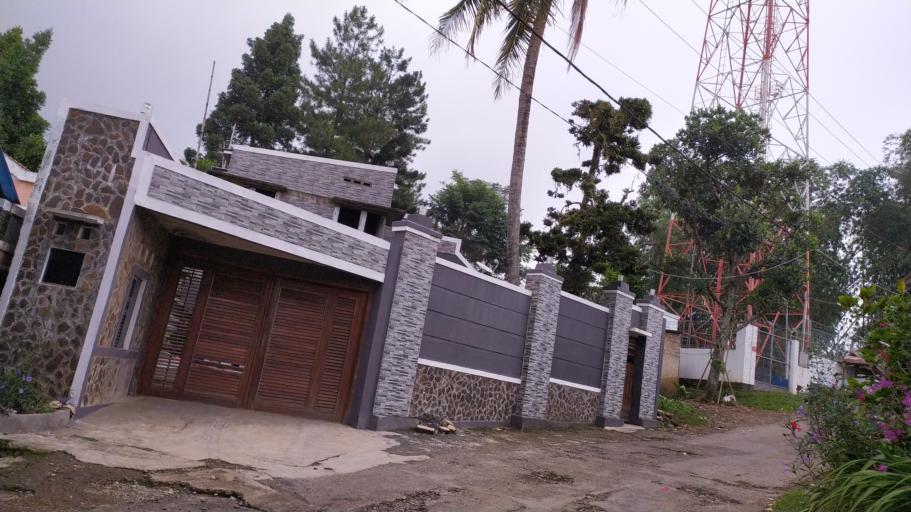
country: ID
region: West Java
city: Ciampea
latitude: -6.6416
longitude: 106.7059
